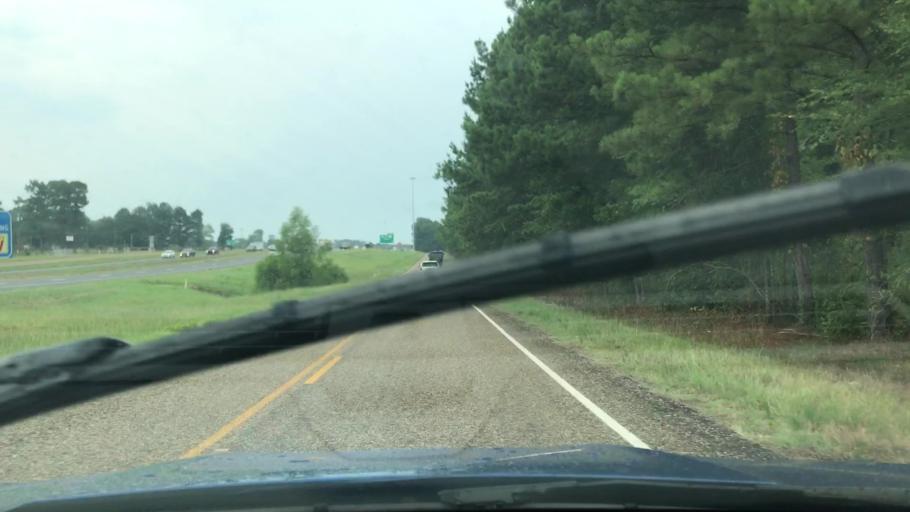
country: US
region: Texas
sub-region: Harrison County
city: Waskom
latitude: 32.4803
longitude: -94.0969
